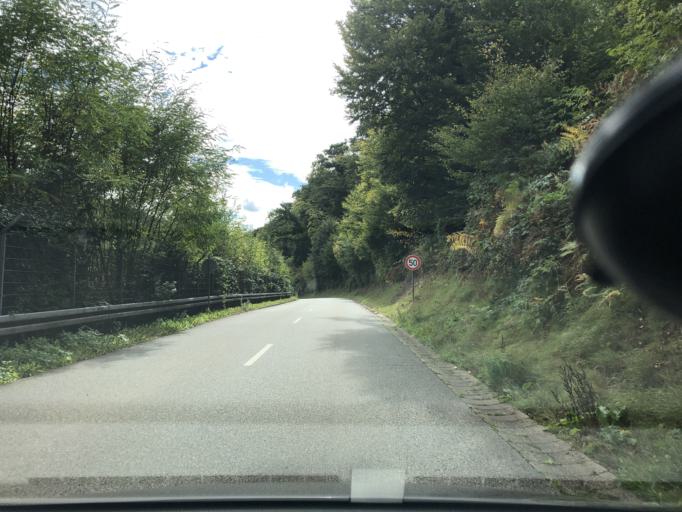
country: DE
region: Baden-Wuerttemberg
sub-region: Karlsruhe Region
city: Eberbach
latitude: 49.4665
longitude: 8.9617
